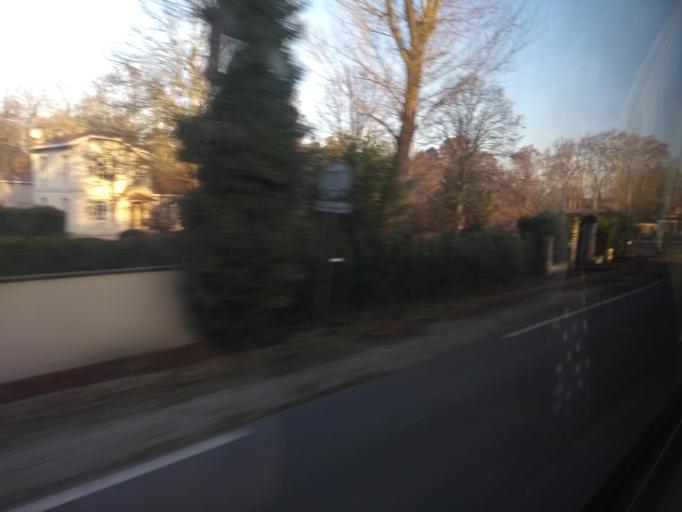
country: FR
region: Aquitaine
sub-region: Departement de la Gironde
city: Gradignan
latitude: 44.7634
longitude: -0.6206
